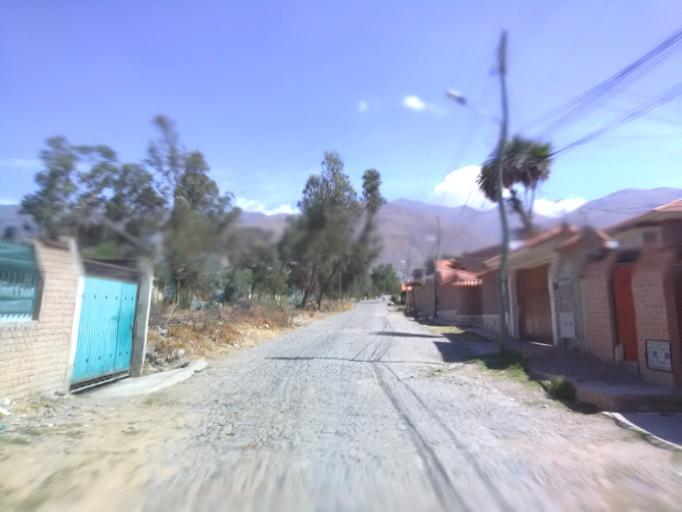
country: BO
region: Cochabamba
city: Cochabamba
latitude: -17.3502
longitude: -66.2005
